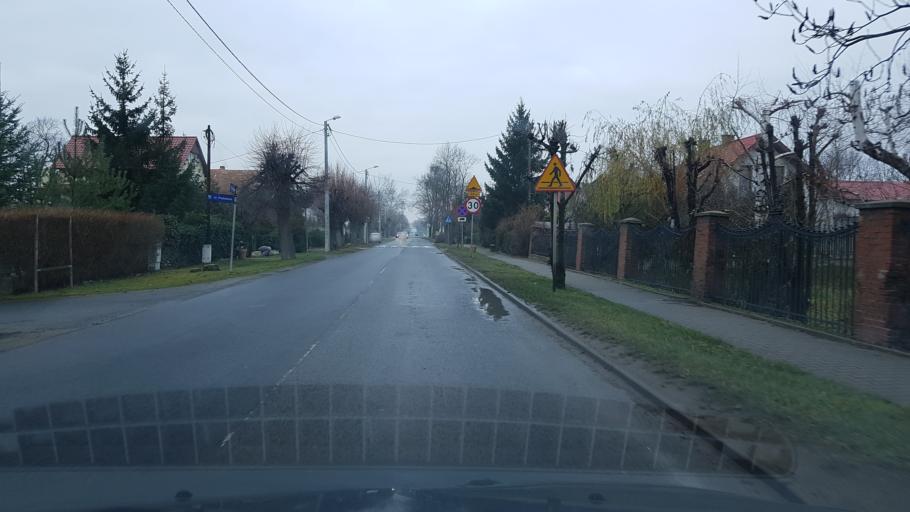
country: PL
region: Lower Silesian Voivodeship
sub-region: Powiat wroclawski
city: Bielany Wroclawskie
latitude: 50.9977
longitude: 16.9808
